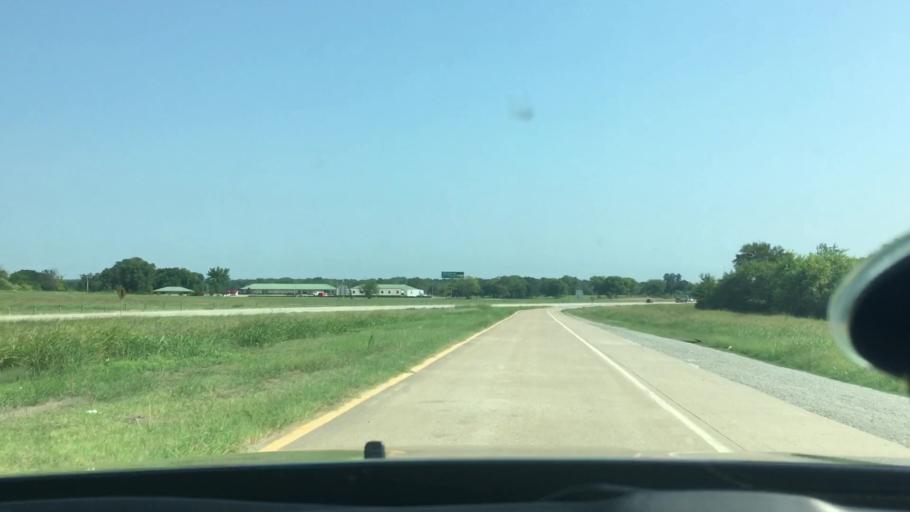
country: US
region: Oklahoma
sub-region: Bryan County
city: Durant
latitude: 34.0517
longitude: -96.3563
